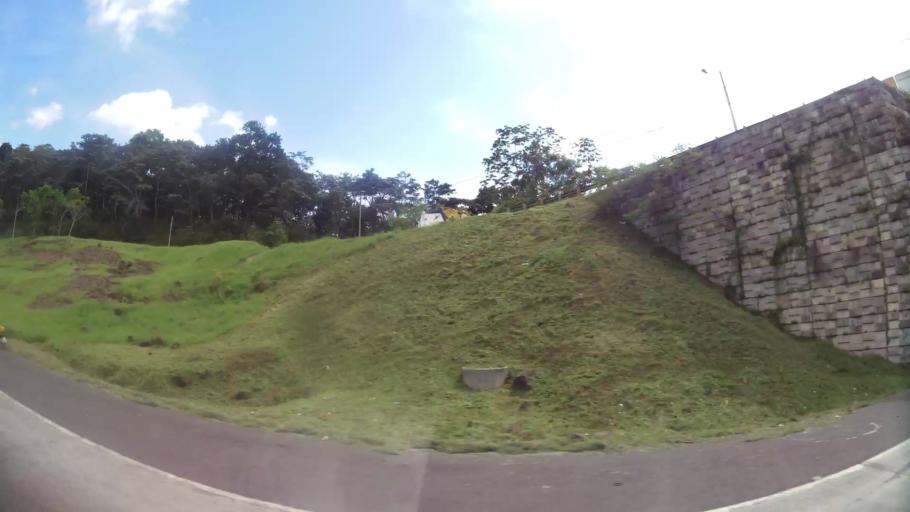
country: PA
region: Panama
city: Las Cumbres
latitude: 9.0399
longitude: -79.5500
